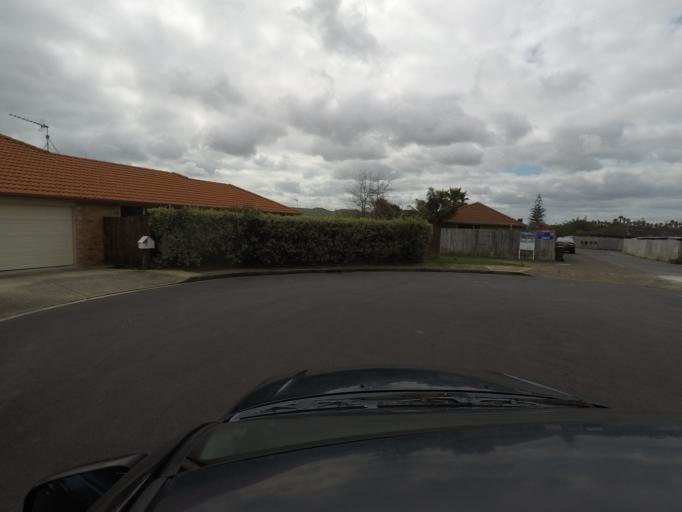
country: NZ
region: Auckland
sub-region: Auckland
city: Tamaki
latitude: -36.9328
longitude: 174.8561
